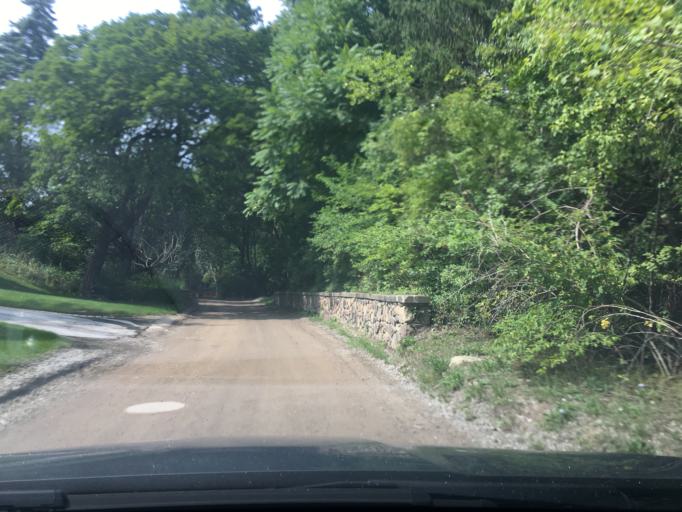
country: US
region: Michigan
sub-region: Oakland County
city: Bloomfield Hills
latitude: 42.5763
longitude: -83.2335
